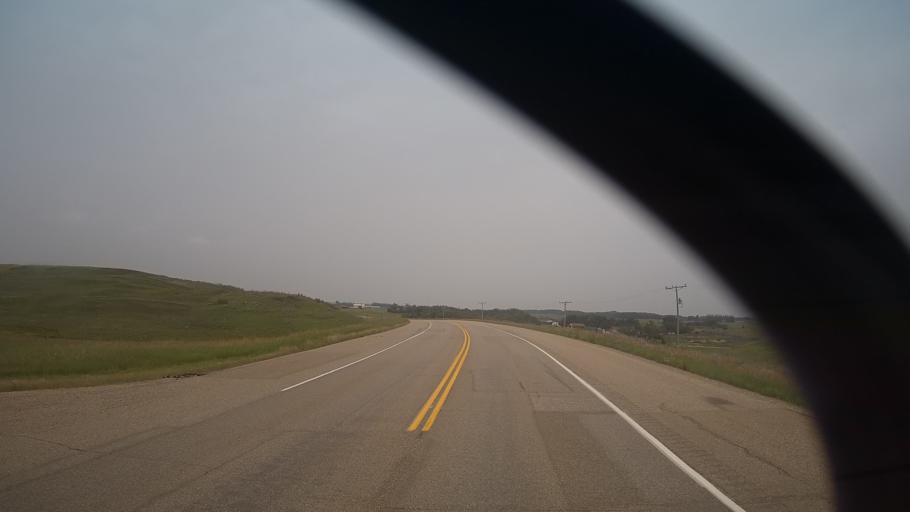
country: CA
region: Saskatchewan
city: Biggar
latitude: 52.0583
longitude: -107.8873
